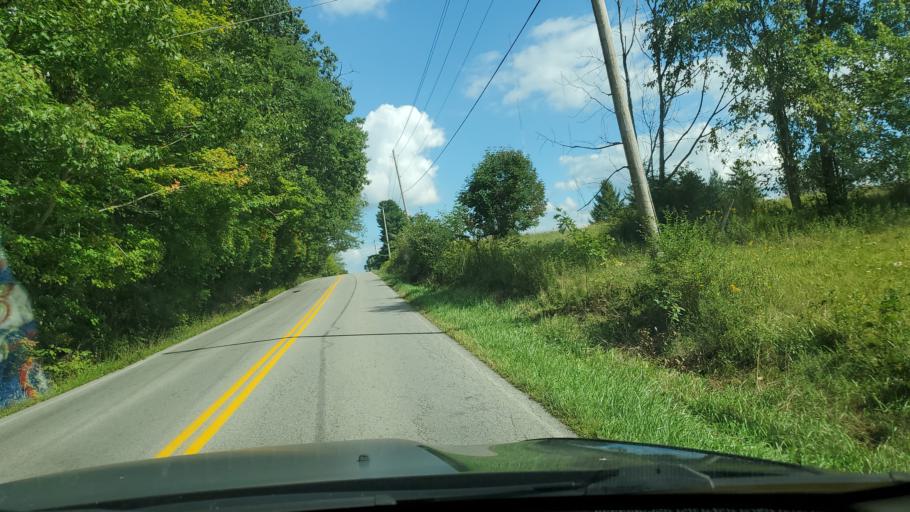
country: US
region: Ohio
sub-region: Mahoning County
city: Poland
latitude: 40.9879
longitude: -80.6033
